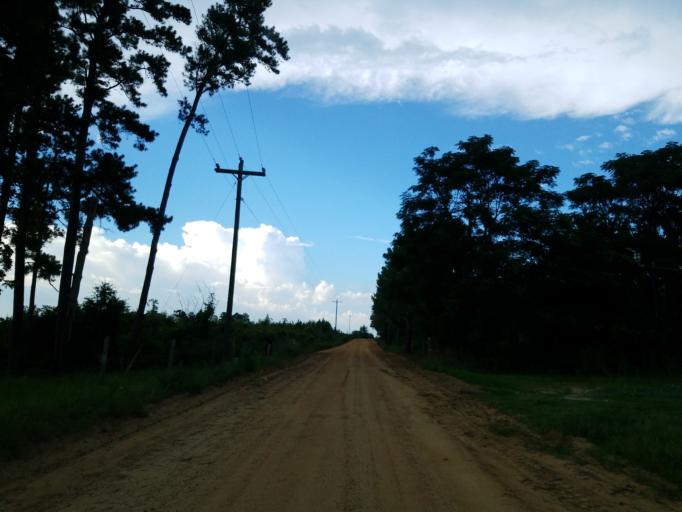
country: US
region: Georgia
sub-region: Tift County
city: Omega
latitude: 31.2685
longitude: -83.5295
